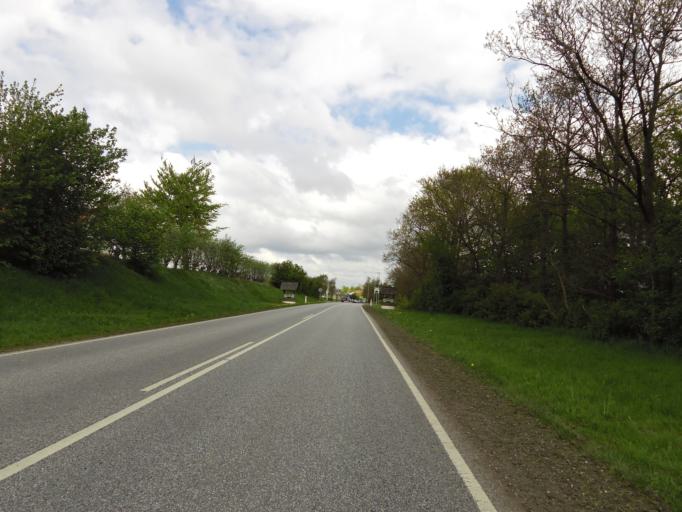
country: DK
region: South Denmark
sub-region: Haderslev Kommune
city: Gram
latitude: 55.2428
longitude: 8.9671
